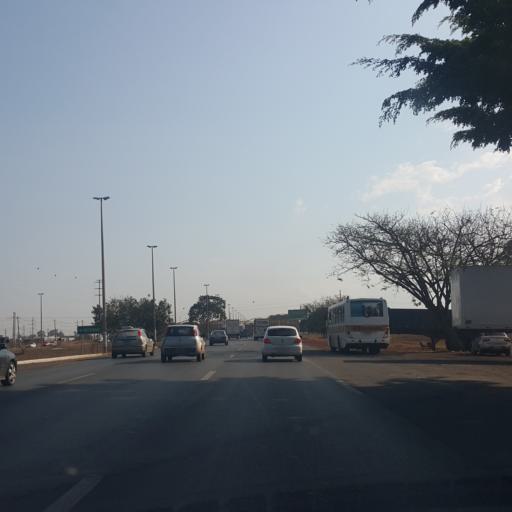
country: BR
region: Federal District
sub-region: Brasilia
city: Brasilia
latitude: -15.8759
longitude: -48.0487
